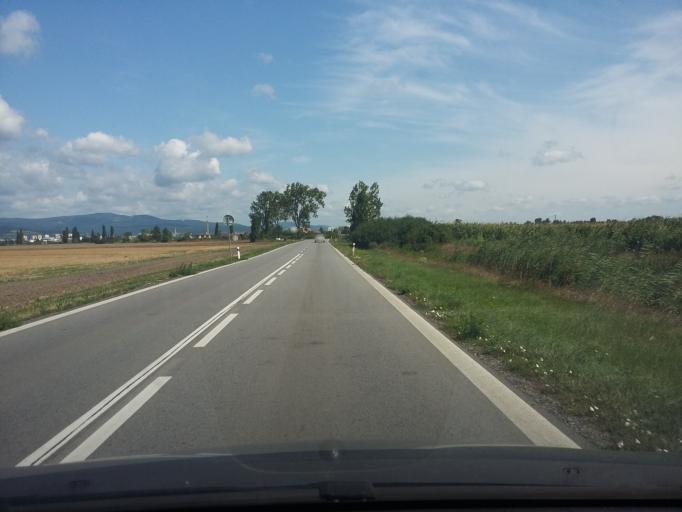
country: SK
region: Bratislavsky
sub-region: Okres Pezinok
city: Pezinok
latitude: 48.2473
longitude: 17.2609
